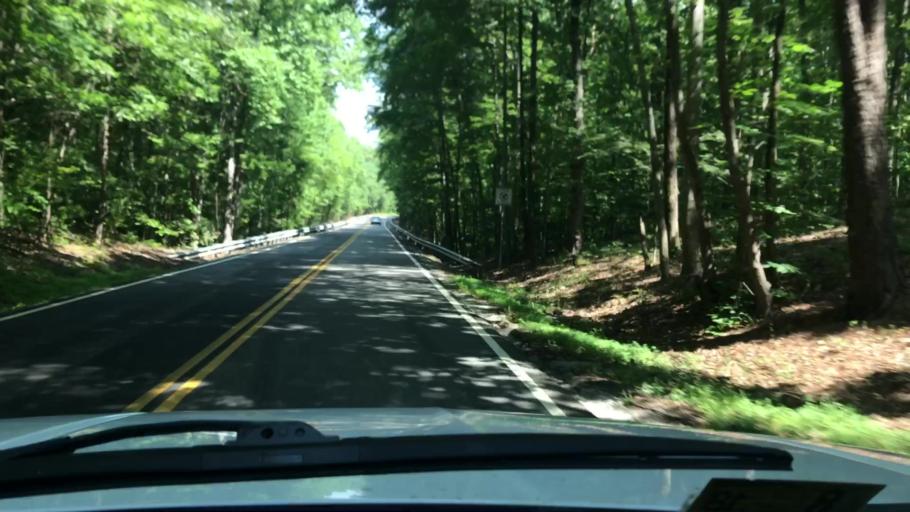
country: US
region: Virginia
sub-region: Henrico County
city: Short Pump
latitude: 37.6040
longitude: -77.6978
